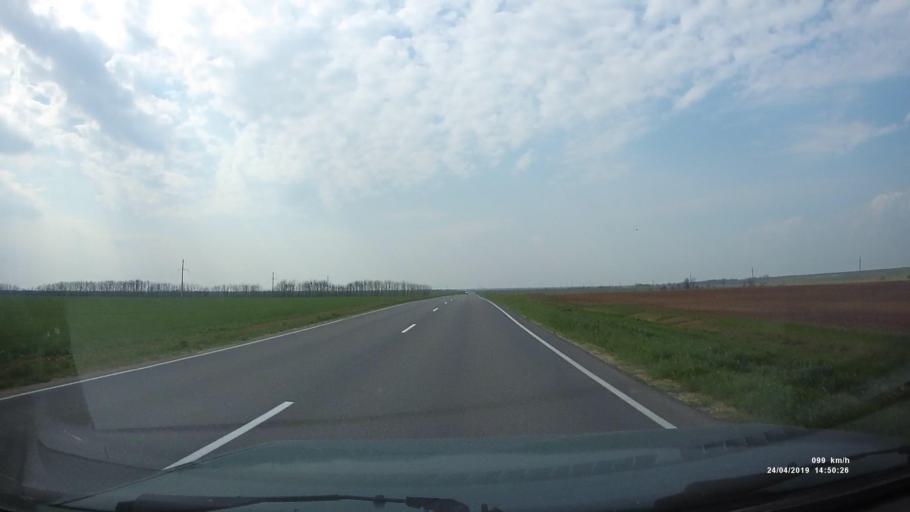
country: RU
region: Rostov
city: Remontnoye
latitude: 46.5173
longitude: 43.7196
